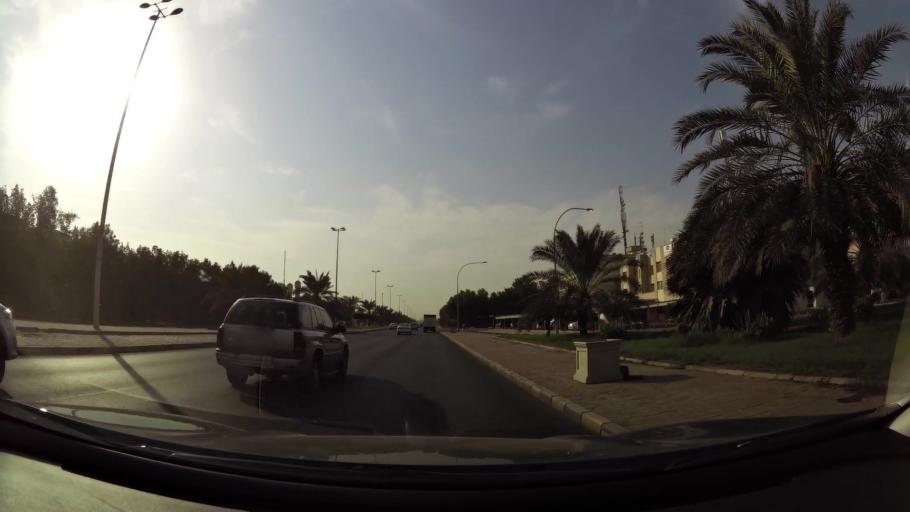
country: KW
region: Muhafazat Hawalli
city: Salwa
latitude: 29.2865
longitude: 48.0863
